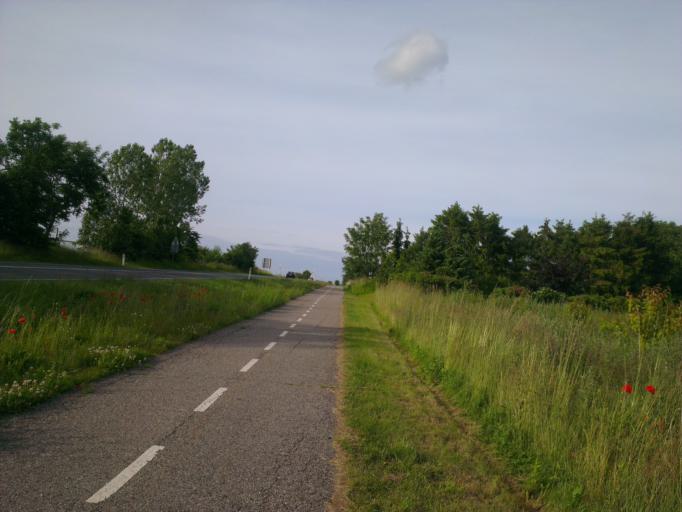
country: DK
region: Capital Region
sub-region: Frederikssund Kommune
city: Skibby
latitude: 55.7842
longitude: 11.9721
